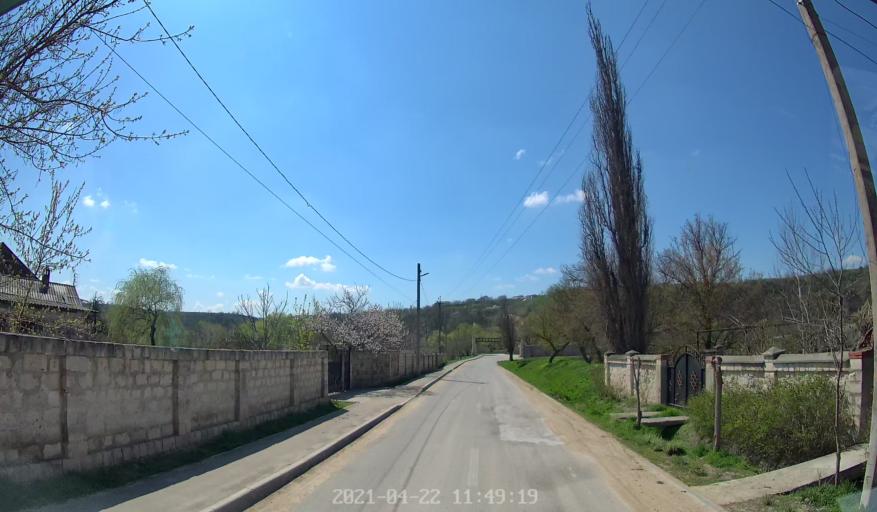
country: MD
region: Chisinau
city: Ciorescu
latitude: 47.1430
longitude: 28.8977
